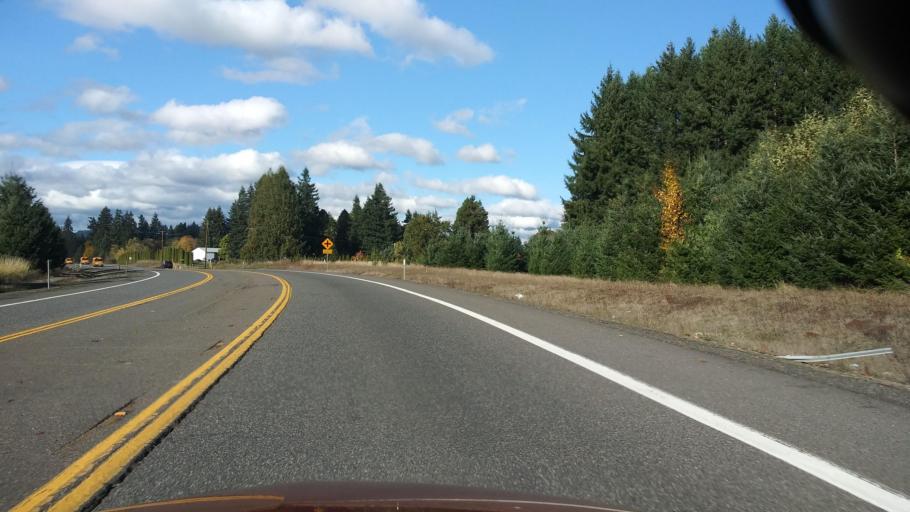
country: US
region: Oregon
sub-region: Washington County
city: Cornelius
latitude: 45.5274
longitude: -123.0850
